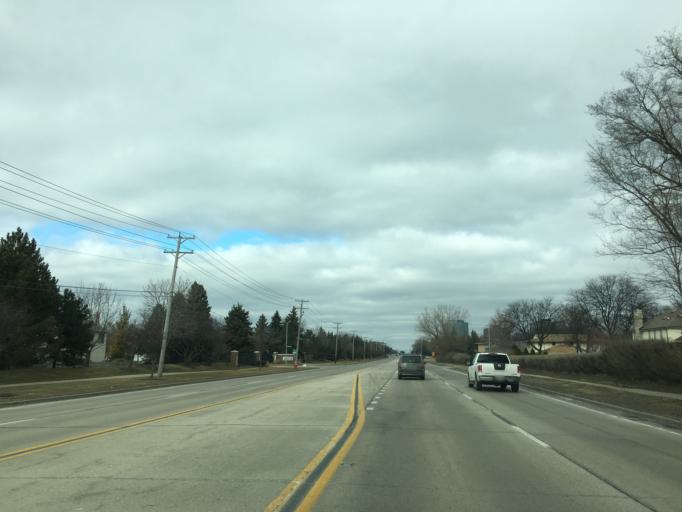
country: US
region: Illinois
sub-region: Cook County
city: Hoffman Estates
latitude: 42.0317
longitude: -88.0455
